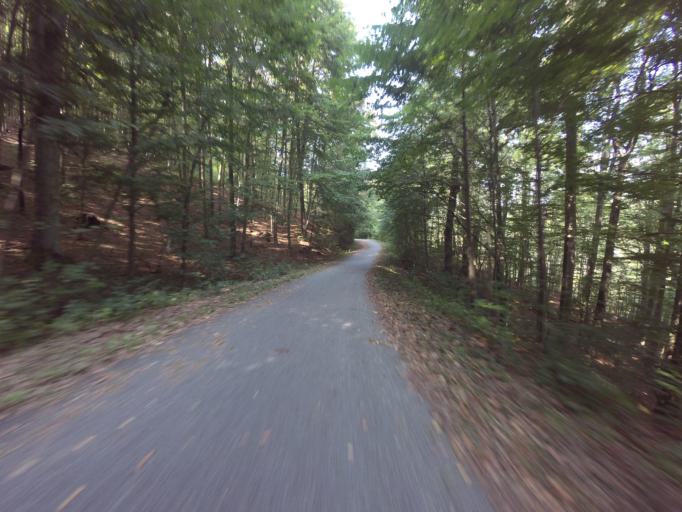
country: CZ
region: Jihocesky
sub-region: Okres Ceske Budejovice
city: Hluboka nad Vltavou
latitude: 49.0912
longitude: 14.4623
